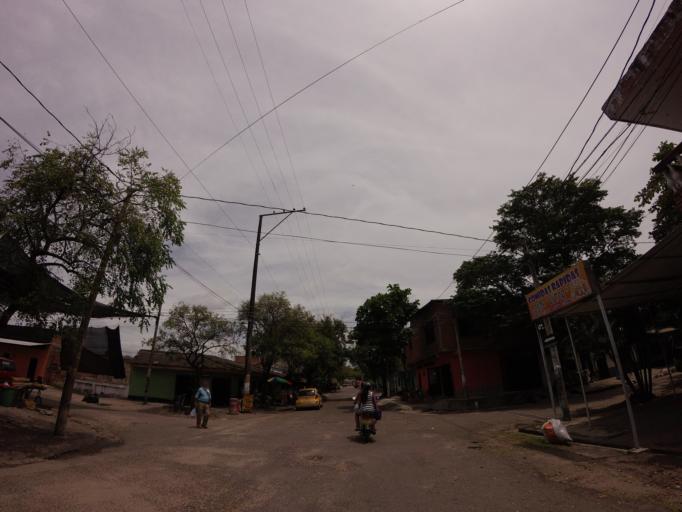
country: CO
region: Caldas
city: La Dorada
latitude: 5.4558
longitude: -74.6660
